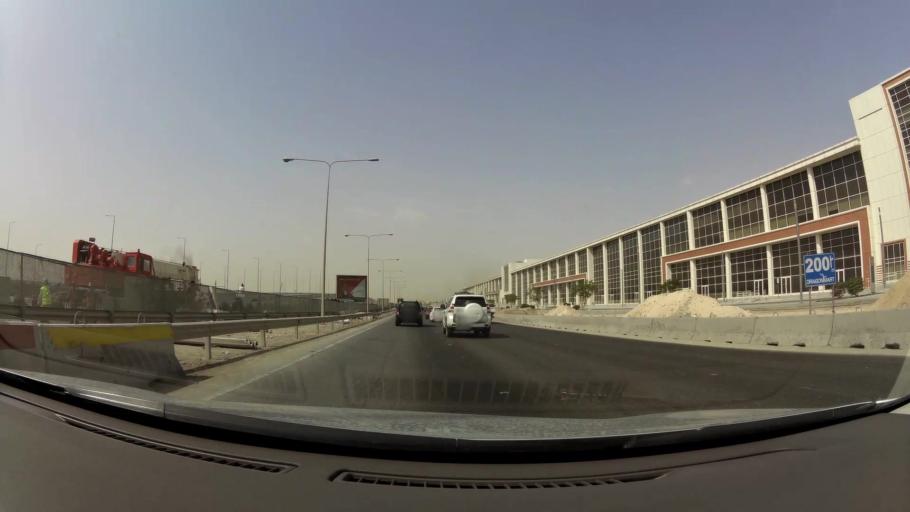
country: QA
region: Al Wakrah
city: Al Wukayr
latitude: 25.1953
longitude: 51.4594
